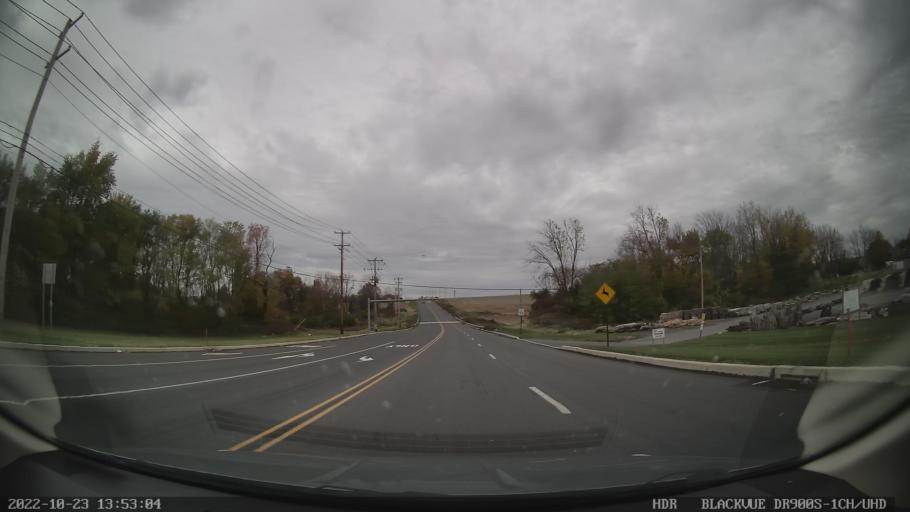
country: US
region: Pennsylvania
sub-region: Lehigh County
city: Catasauqua
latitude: 40.6588
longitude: -75.4464
